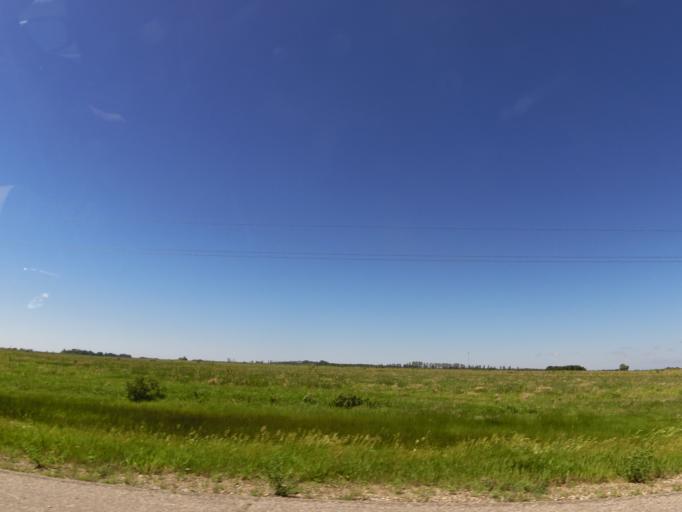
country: US
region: Minnesota
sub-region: Red Lake County
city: Red Lake Falls
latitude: 47.7518
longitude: -96.2468
